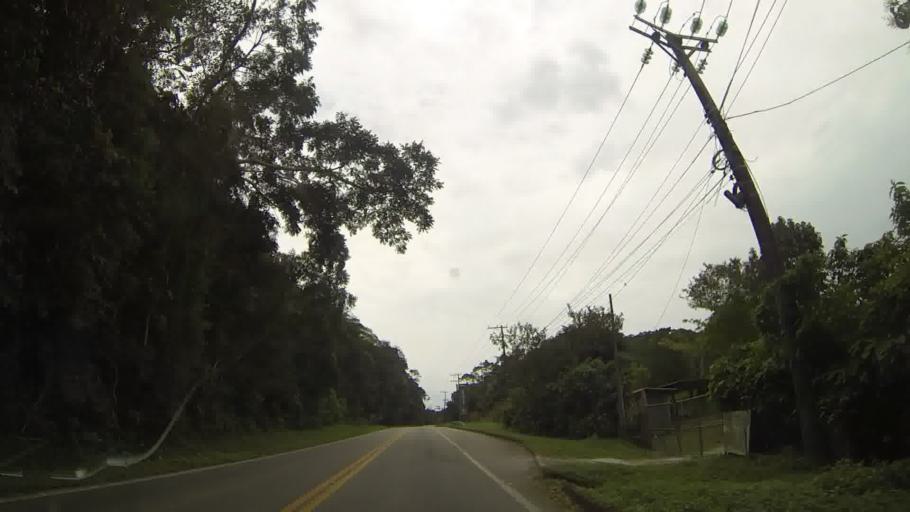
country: BR
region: Sao Paulo
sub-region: Sao Sebastiao
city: Sao Sebastiao
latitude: -23.8251
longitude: -45.4854
